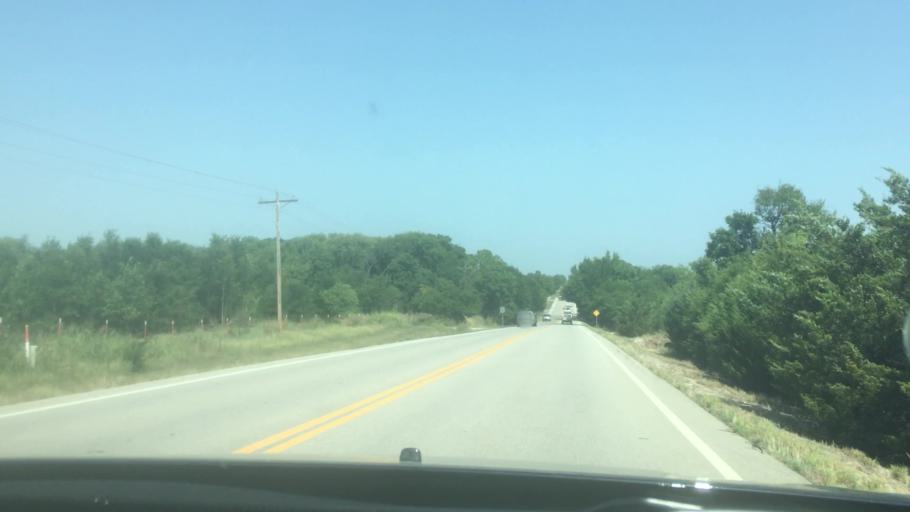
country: US
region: Oklahoma
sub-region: Bryan County
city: Durant
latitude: 34.1550
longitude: -96.3854
